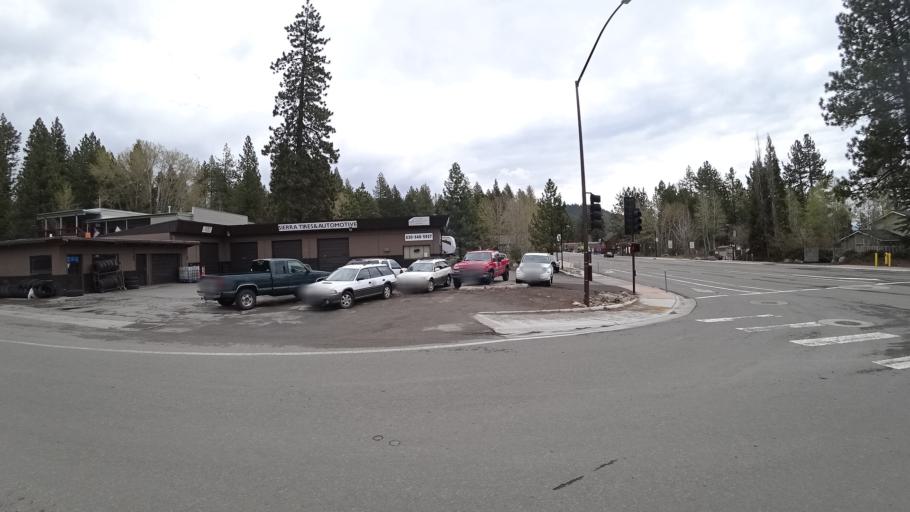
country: US
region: California
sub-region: Placer County
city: Kings Beach
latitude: 39.2381
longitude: -120.0316
